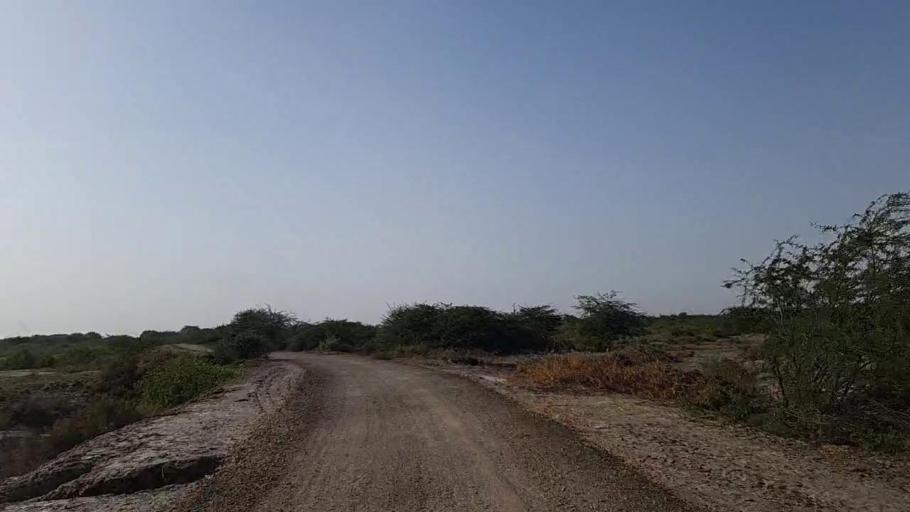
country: PK
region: Sindh
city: Jati
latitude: 24.2872
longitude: 68.2112
